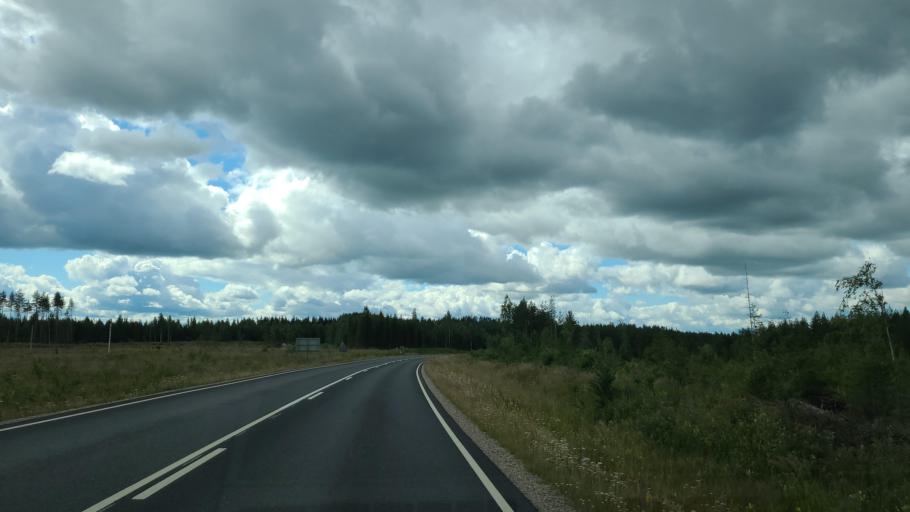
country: FI
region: Northern Savo
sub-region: Koillis-Savo
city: Kaavi
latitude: 62.9342
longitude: 28.3748
